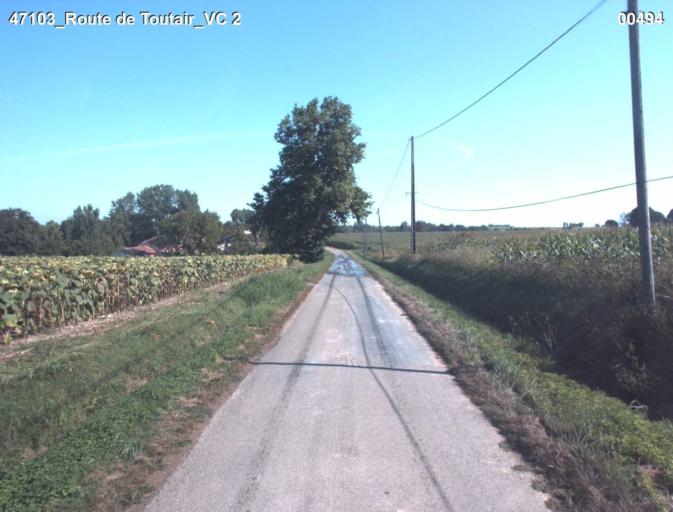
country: FR
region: Aquitaine
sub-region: Departement du Lot-et-Garonne
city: Nerac
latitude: 44.0808
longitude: 0.3217
